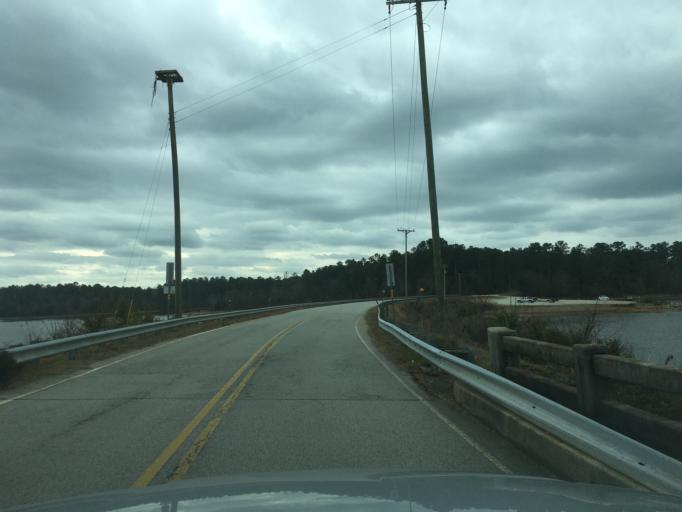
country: US
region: Georgia
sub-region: Lincoln County
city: Lincolnton
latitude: 33.8282
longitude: -82.4040
